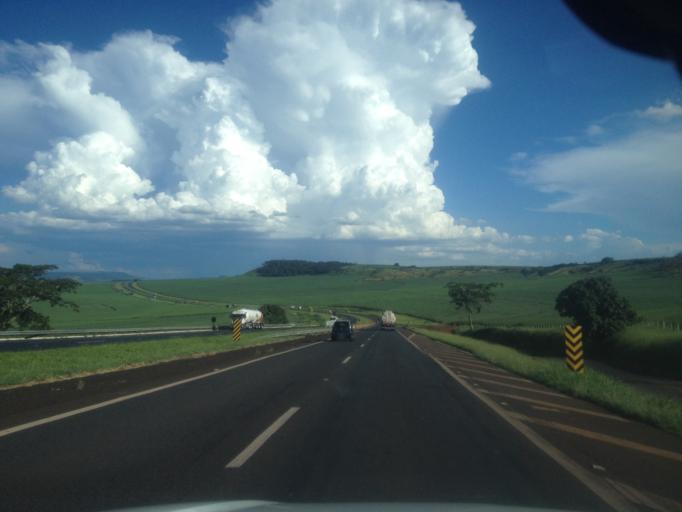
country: BR
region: Sao Paulo
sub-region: Cravinhos
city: Cravinhos
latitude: -21.3874
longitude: -47.6995
